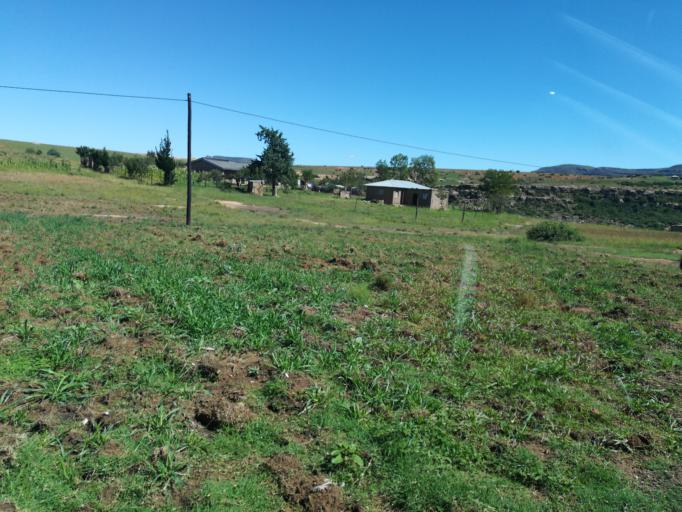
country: LS
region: Quthing
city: Quthing
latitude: -30.3377
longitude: 27.5300
